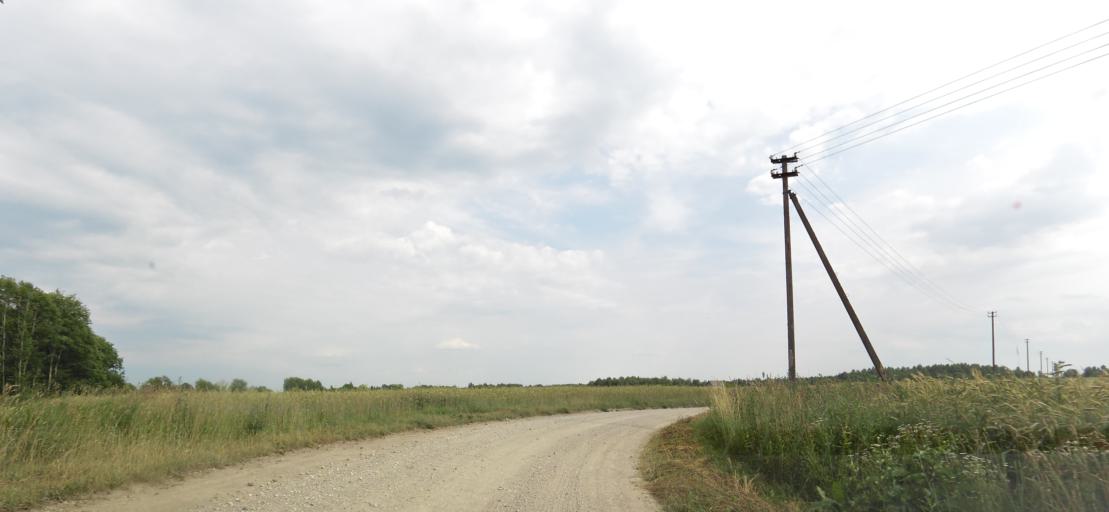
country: LT
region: Panevezys
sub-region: Birzai
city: Birzai
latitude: 56.1832
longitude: 24.9849
